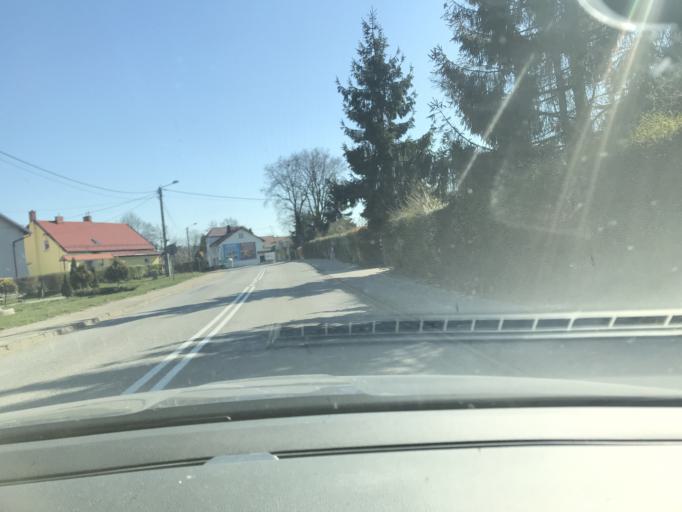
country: PL
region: Pomeranian Voivodeship
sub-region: Powiat nowodworski
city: Sztutowo
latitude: 54.3283
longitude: 19.1787
